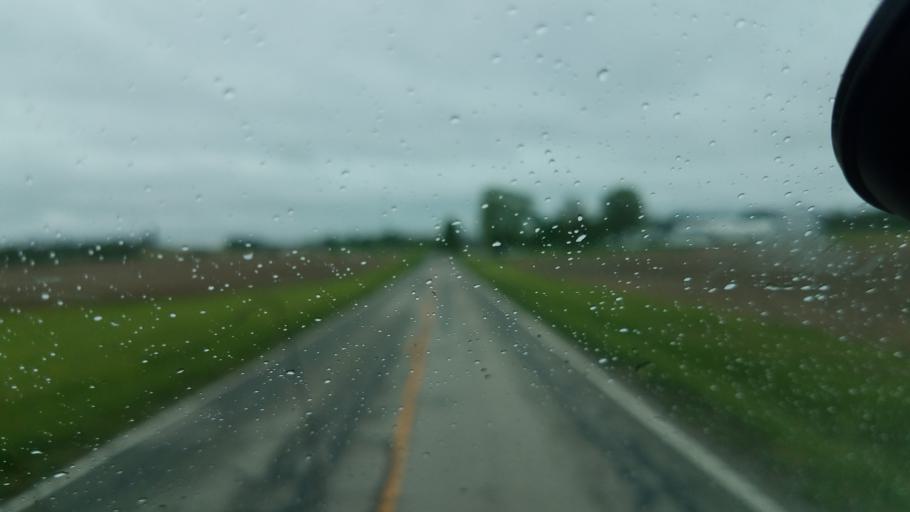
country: US
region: Ohio
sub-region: Highland County
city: Leesburg
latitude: 39.3237
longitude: -83.5577
